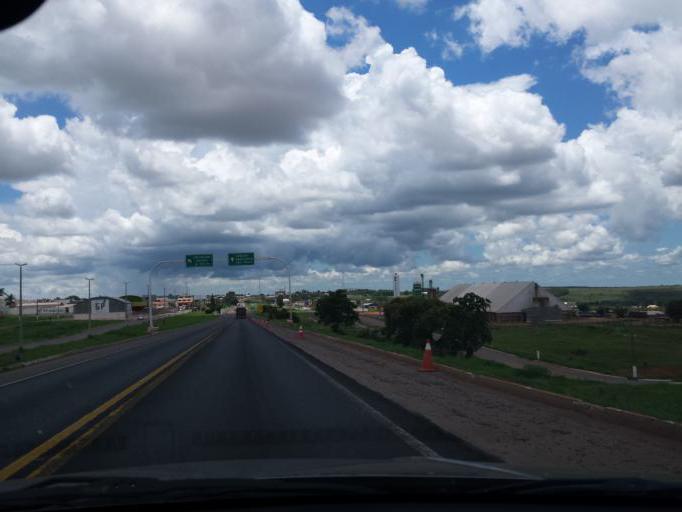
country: BR
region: Goias
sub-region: Cristalina
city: Cristalina
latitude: -16.7590
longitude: -47.6104
